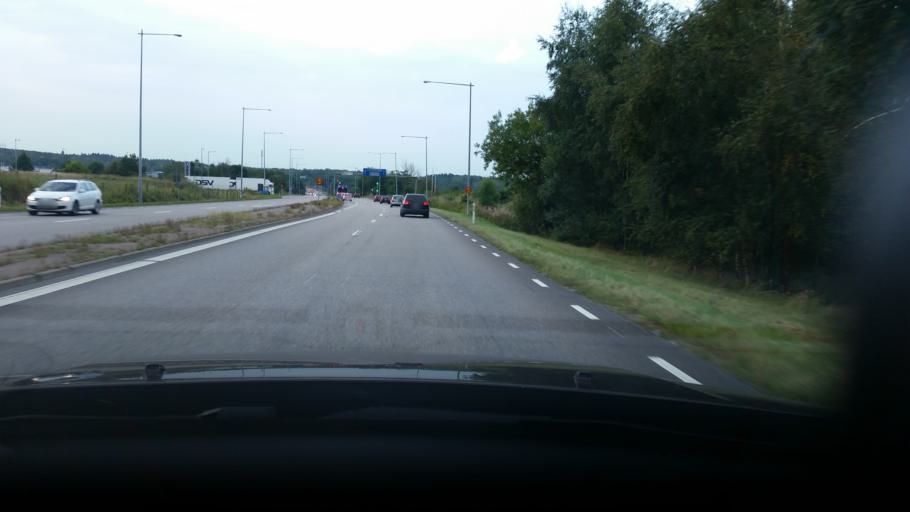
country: SE
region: Vaestra Goetaland
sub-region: Goteborg
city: Majorna
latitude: 57.7581
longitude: 11.8791
